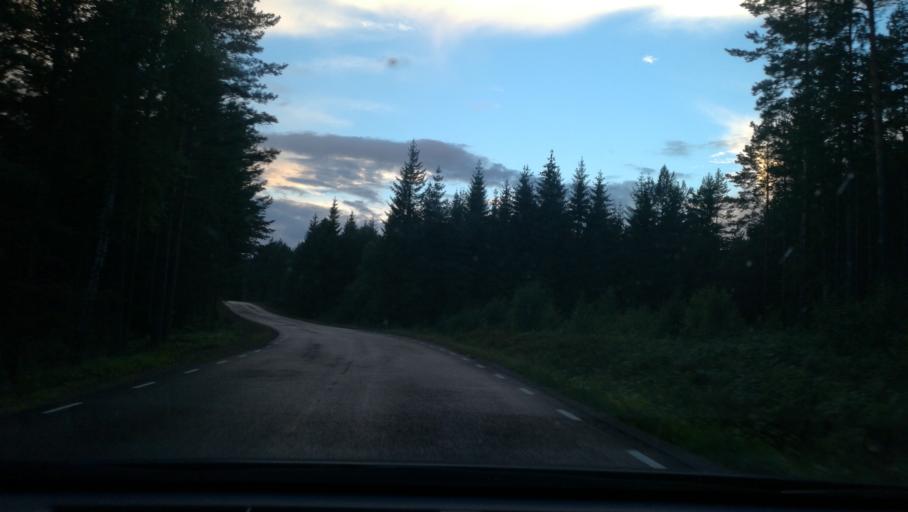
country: SE
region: OEstergoetland
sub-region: Norrkopings Kommun
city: Svartinge
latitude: 58.8203
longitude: 16.0631
